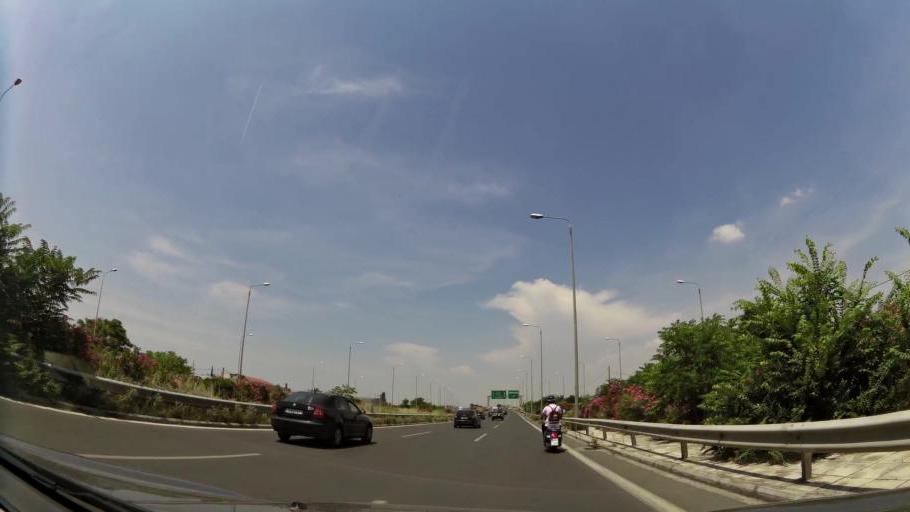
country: GR
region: Central Macedonia
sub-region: Nomos Thessalonikis
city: Menemeni
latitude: 40.6510
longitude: 22.9049
